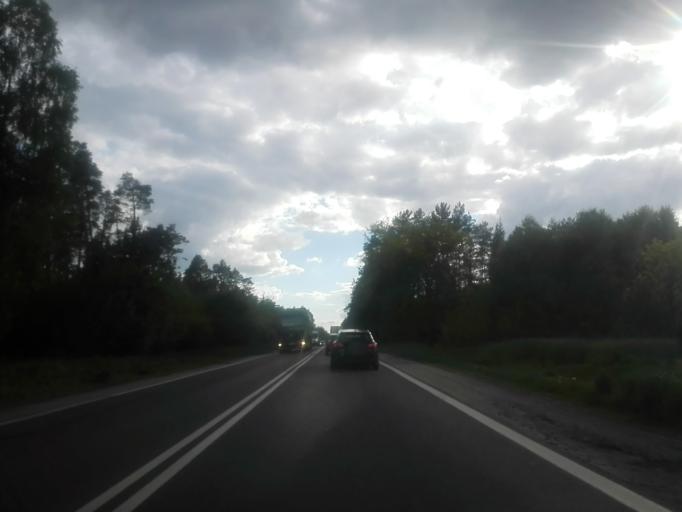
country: PL
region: Masovian Voivodeship
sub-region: Powiat ostrowski
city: Brok
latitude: 52.7492
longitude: 21.7772
